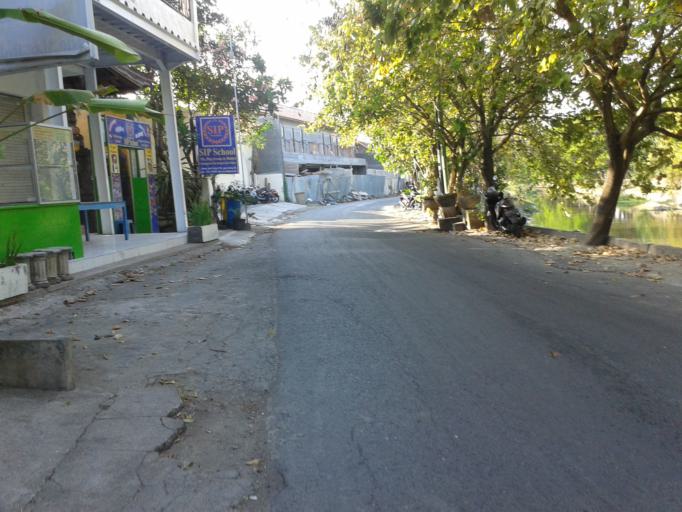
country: ID
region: Bali
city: Kuta
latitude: -8.7036
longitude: 115.1726
